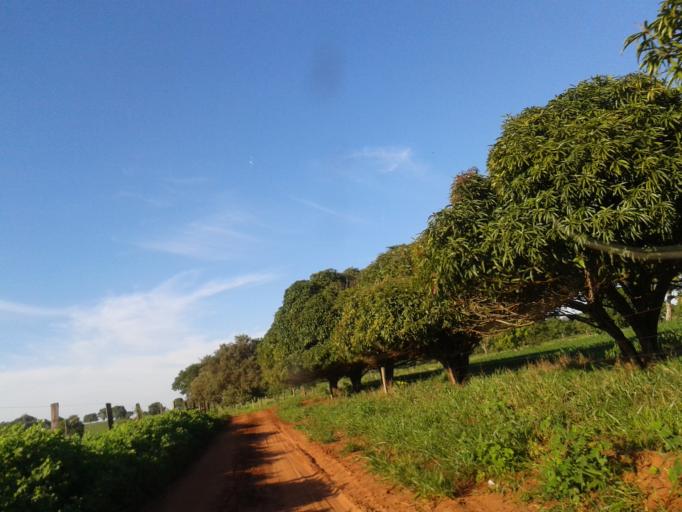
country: BR
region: Minas Gerais
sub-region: Santa Vitoria
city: Santa Vitoria
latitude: -18.9729
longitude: -49.8872
